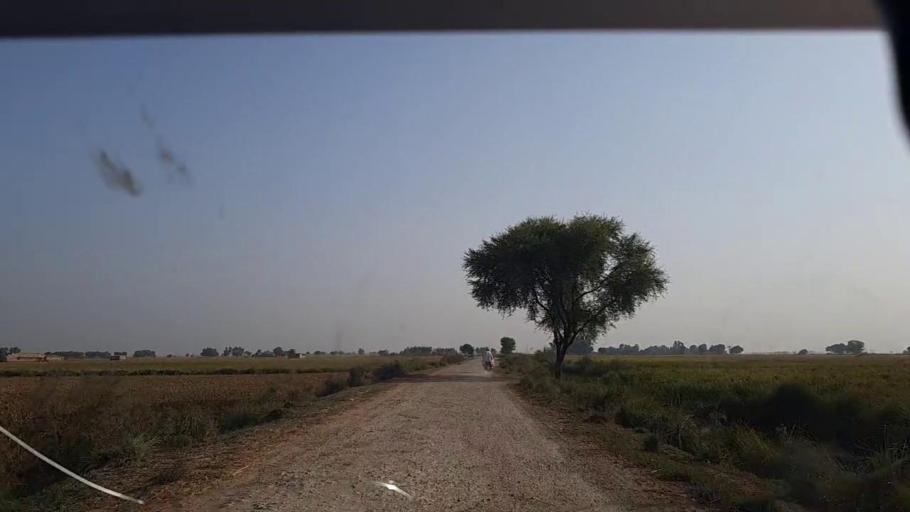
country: PK
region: Sindh
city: Shikarpur
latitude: 28.0686
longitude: 68.5461
